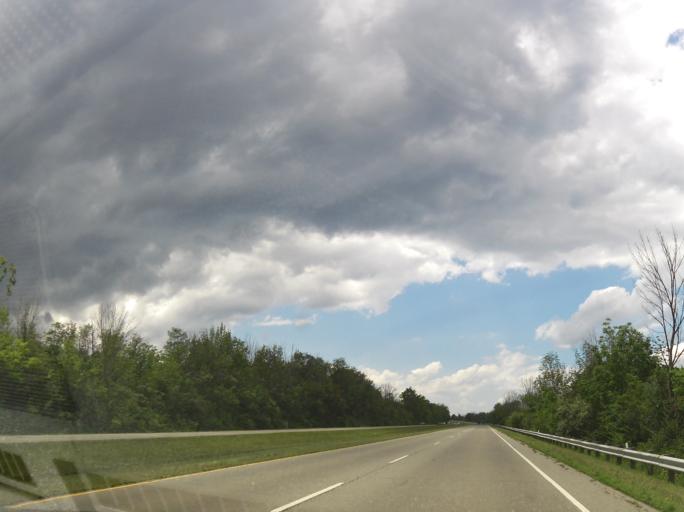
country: US
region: Ohio
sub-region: Greene County
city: Wright-Patterson AFB
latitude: 39.7948
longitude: -84.0744
